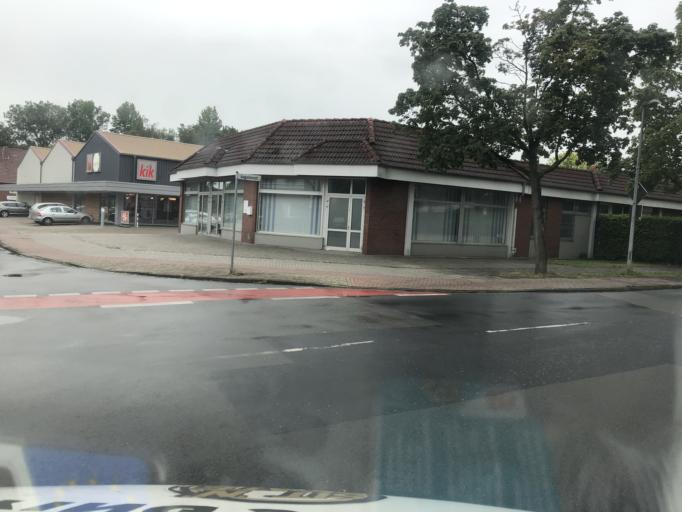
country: DE
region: Lower Saxony
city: Leer
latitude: 53.2410
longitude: 7.4603
